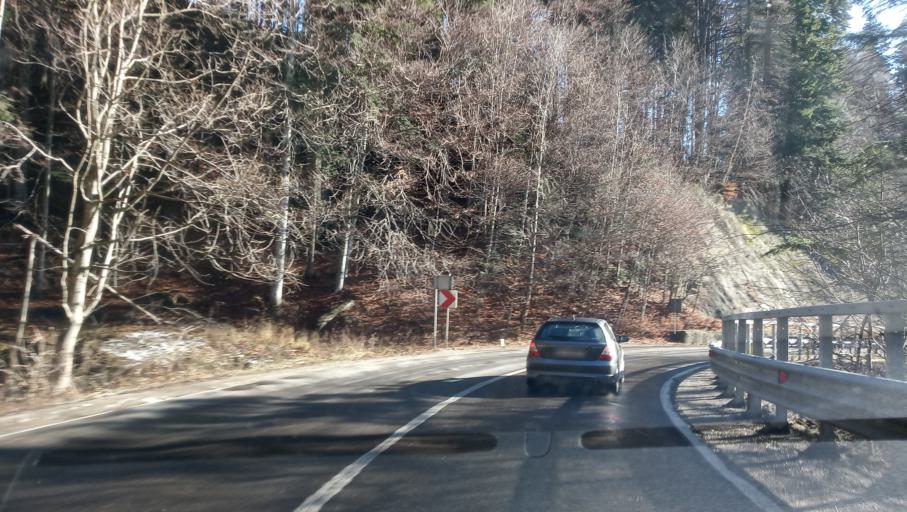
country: RO
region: Brasov
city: Crivina
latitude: 45.4719
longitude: 25.9287
